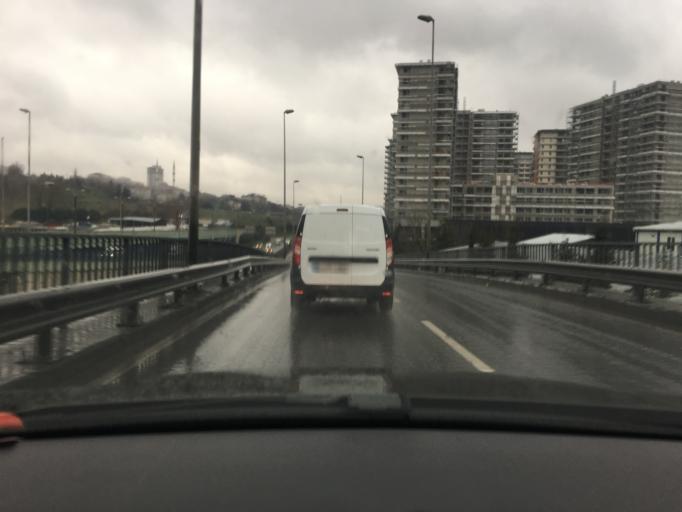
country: TR
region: Istanbul
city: merter keresteciler
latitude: 41.0211
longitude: 28.9006
